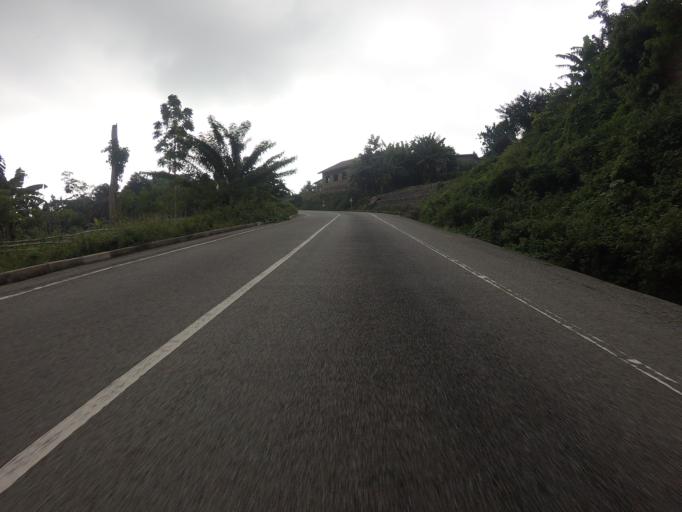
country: GH
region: Volta
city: Kpandu
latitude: 6.8204
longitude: 0.4258
